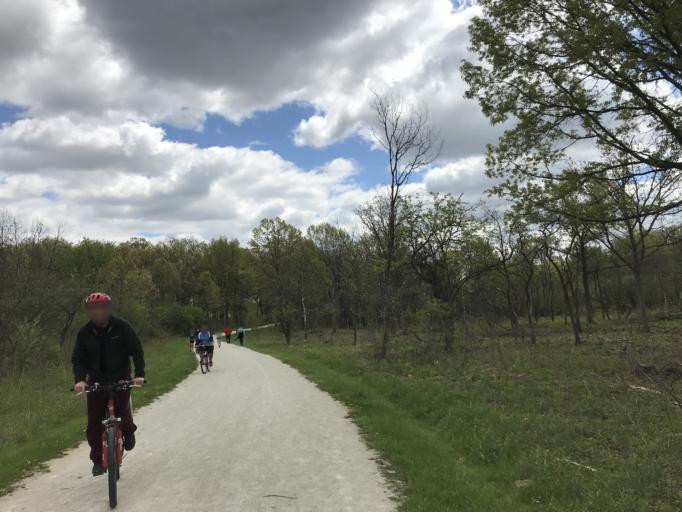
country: US
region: Illinois
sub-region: DuPage County
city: Woodridge
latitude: 41.7359
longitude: -88.0818
